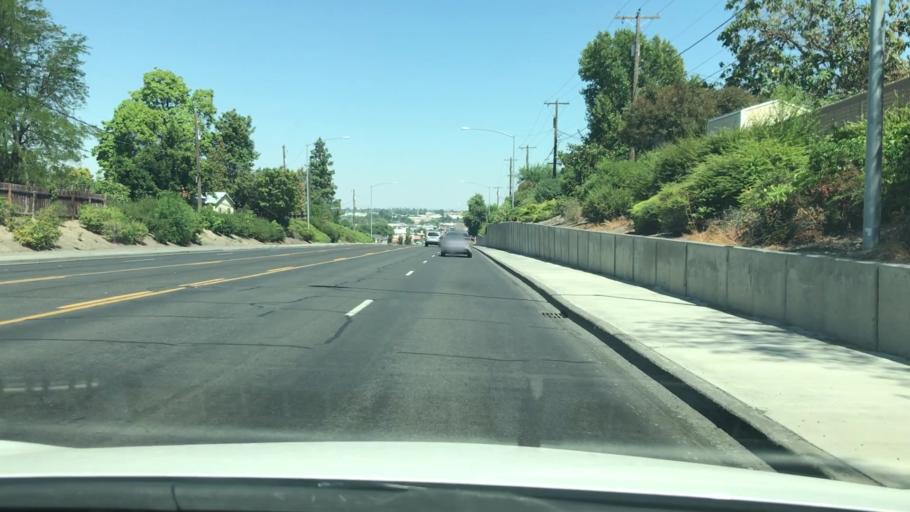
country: US
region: Washington
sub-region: Grant County
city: Moses Lake
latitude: 47.1222
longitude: -119.2678
